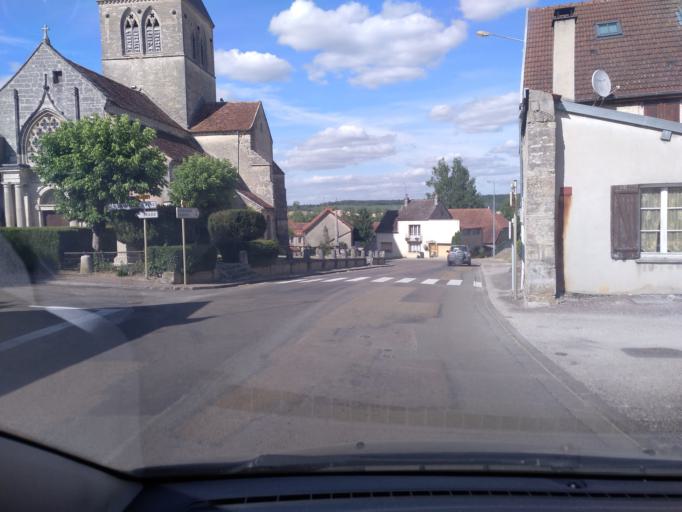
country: FR
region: Bourgogne
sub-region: Departement de la Cote-d'Or
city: Chatillon-sur-Seine
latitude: 47.9428
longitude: 4.6519
